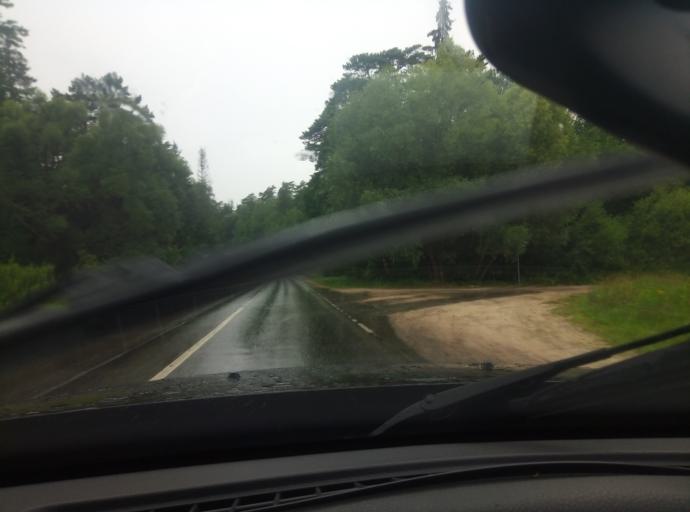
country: RU
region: Moskovskaya
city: Protvino
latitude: 54.8870
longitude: 37.1785
